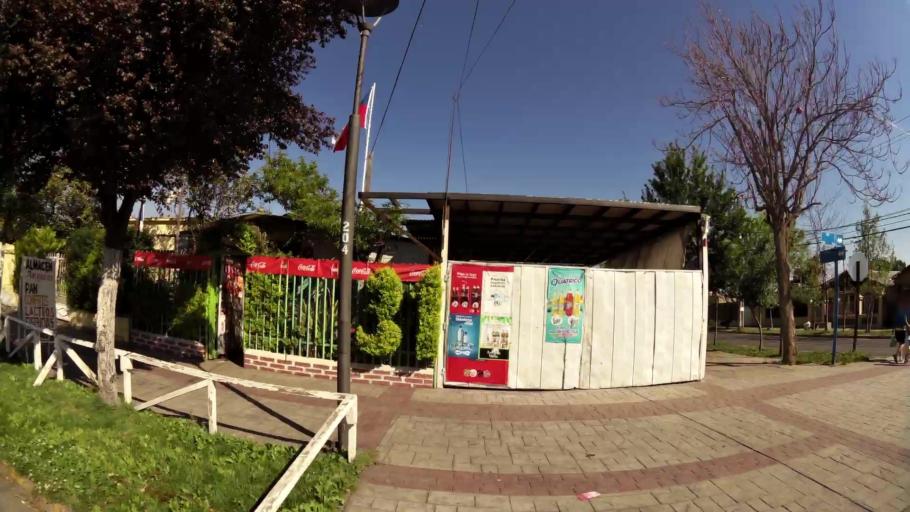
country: CL
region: Santiago Metropolitan
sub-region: Provincia de Santiago
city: La Pintana
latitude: -33.5316
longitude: -70.6164
